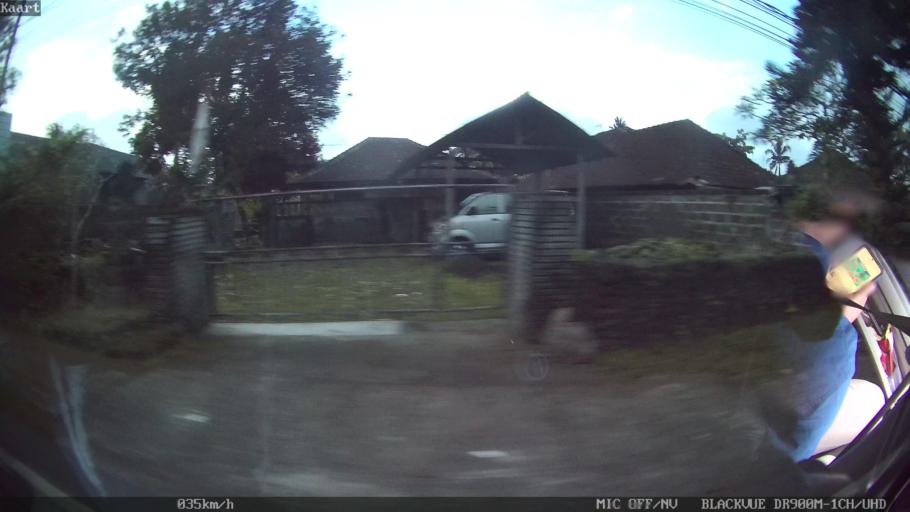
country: ID
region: Bali
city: Bunutan
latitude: -8.4770
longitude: 115.2489
